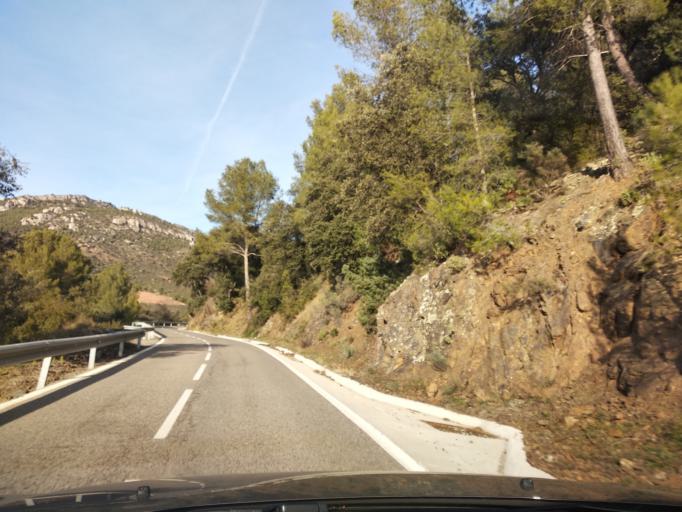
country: ES
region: Catalonia
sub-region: Provincia de Tarragona
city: Margalef
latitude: 41.2392
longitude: 0.7873
